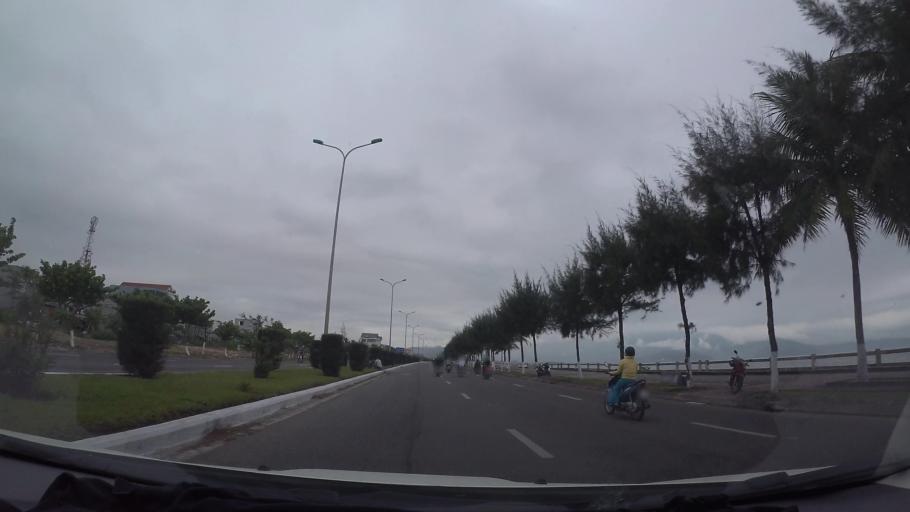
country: VN
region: Da Nang
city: Lien Chieu
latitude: 16.0845
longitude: 108.1607
